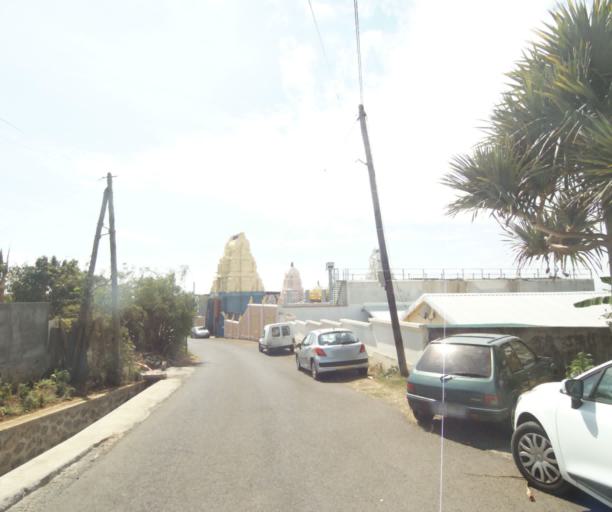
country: RE
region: Reunion
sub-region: Reunion
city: Saint-Paul
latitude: -21.0573
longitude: 55.2613
